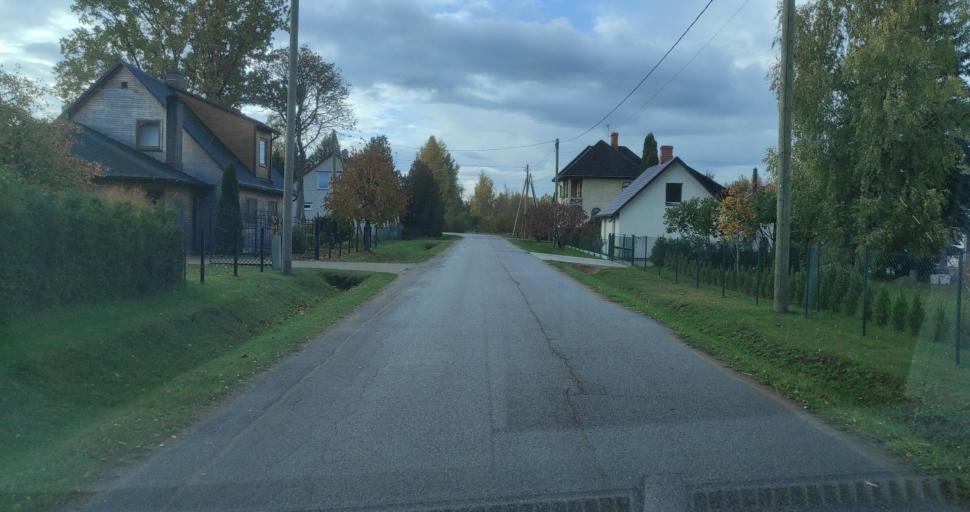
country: LV
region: Skrunda
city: Skrunda
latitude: 56.6708
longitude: 22.0128
